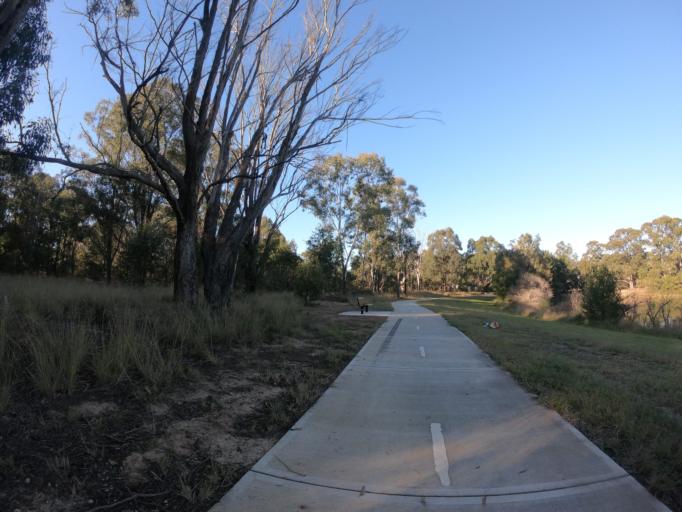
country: AU
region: New South Wales
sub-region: Hawkesbury
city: South Windsor
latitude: -33.6343
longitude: 150.8112
